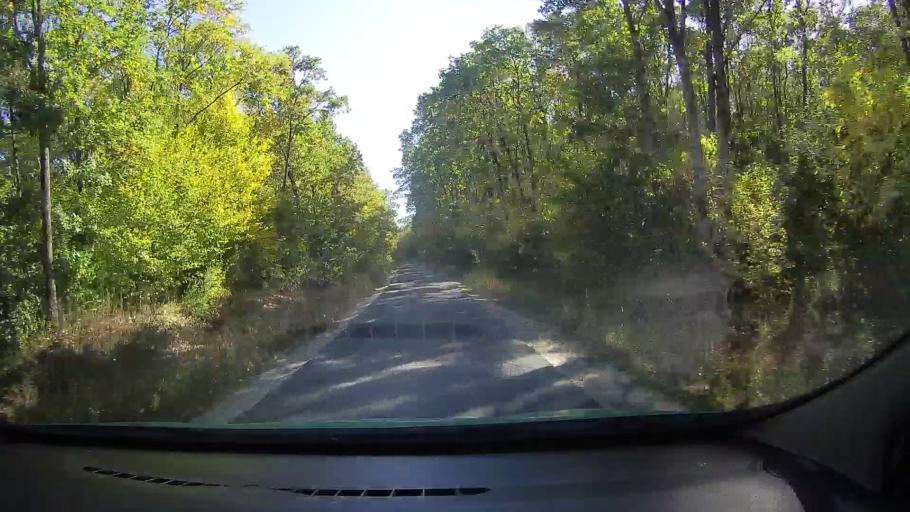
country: RO
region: Satu Mare
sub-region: Comuna Doba
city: Doba
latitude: 47.7099
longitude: 22.7529
